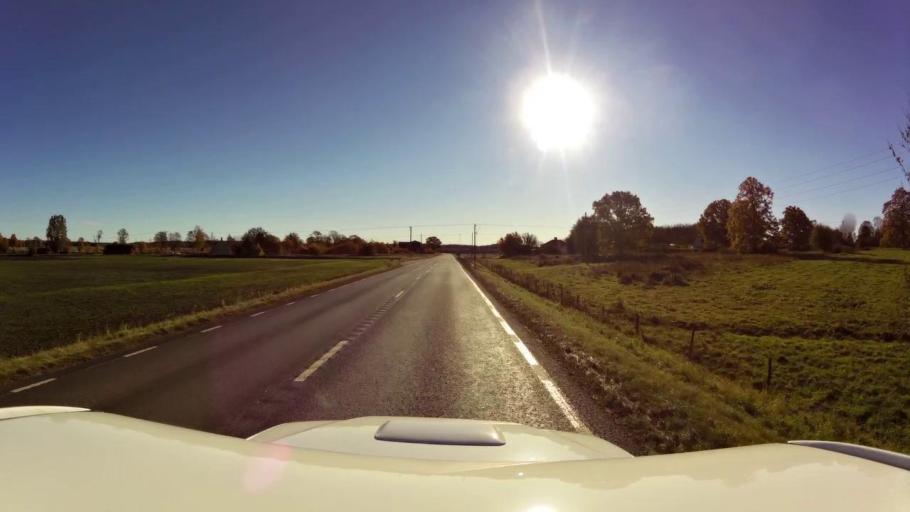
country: SE
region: OEstergoetland
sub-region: Linkopings Kommun
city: Ljungsbro
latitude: 58.5214
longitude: 15.4221
